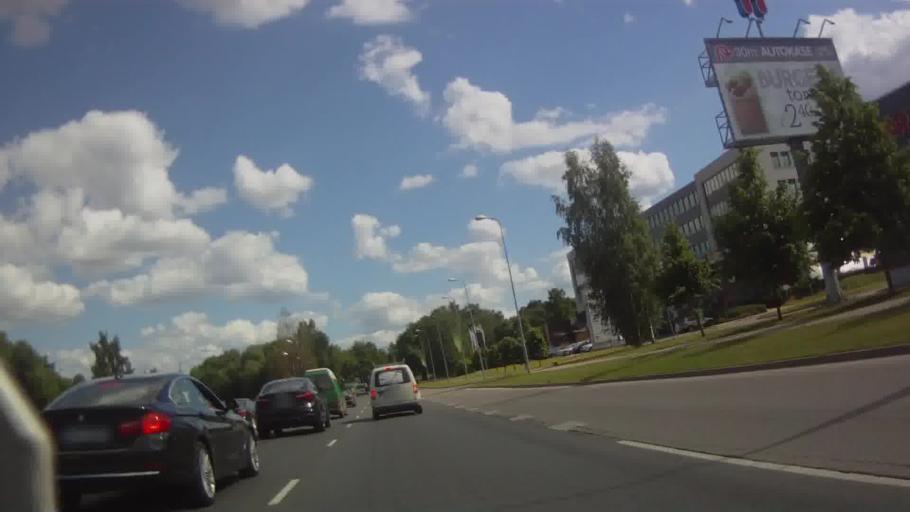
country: LV
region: Riga
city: Riga
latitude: 56.9159
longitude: 24.1195
